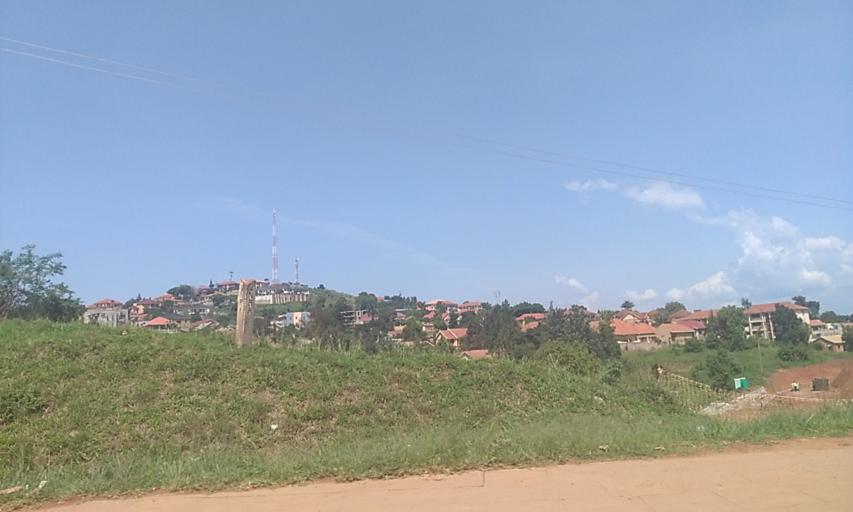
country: UG
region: Central Region
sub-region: Wakiso District
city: Kireka
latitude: 0.3658
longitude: 32.6049
